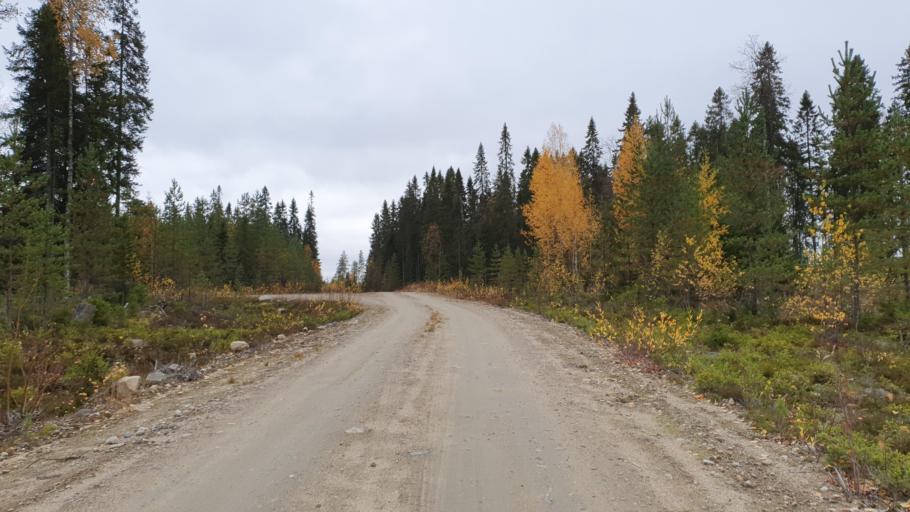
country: FI
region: Kainuu
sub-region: Kehys-Kainuu
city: Kuhmo
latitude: 64.4507
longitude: 29.6085
